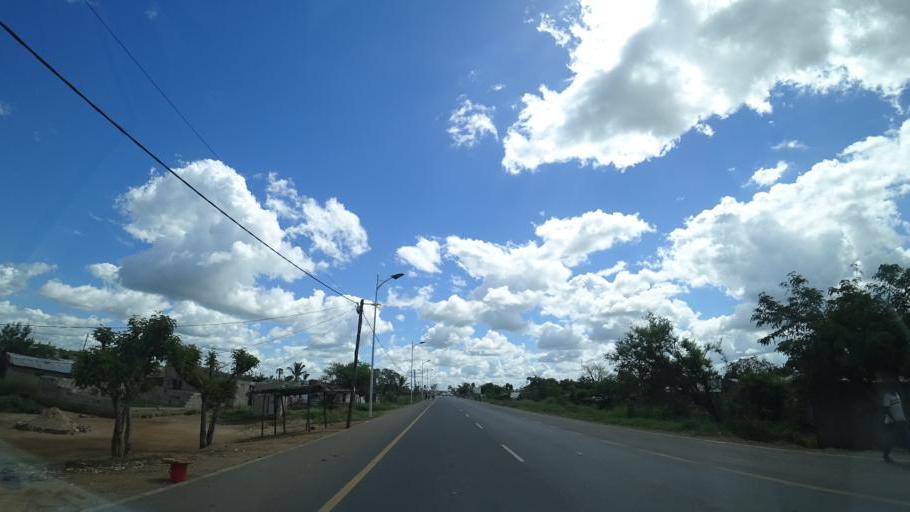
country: MZ
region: Sofala
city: Dondo
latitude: -19.2731
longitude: 34.2124
